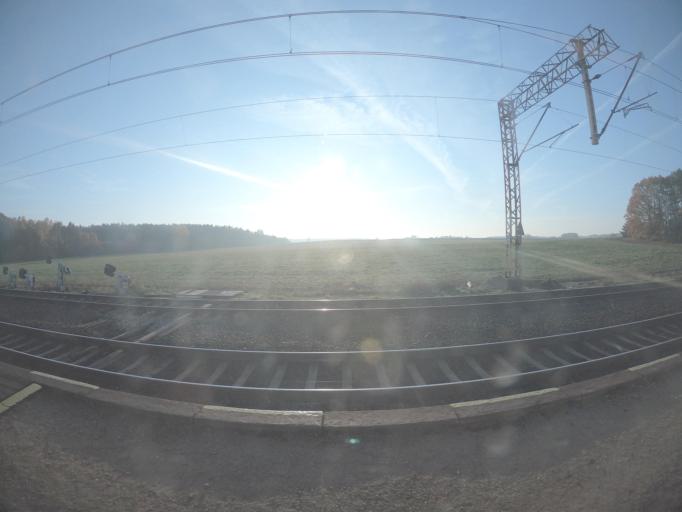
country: PL
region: Lubusz
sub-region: Powiat sulecinski
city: Torzym
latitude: 52.2462
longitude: 14.9636
